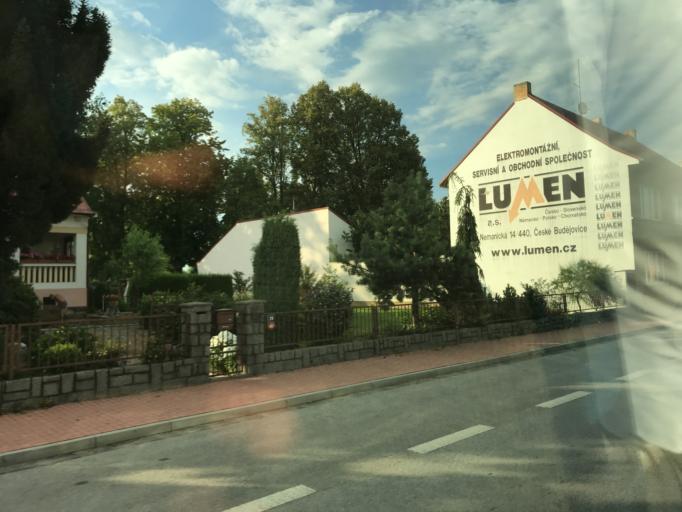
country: CZ
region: Jihocesky
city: Lisov
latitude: 49.0138
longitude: 14.5972
